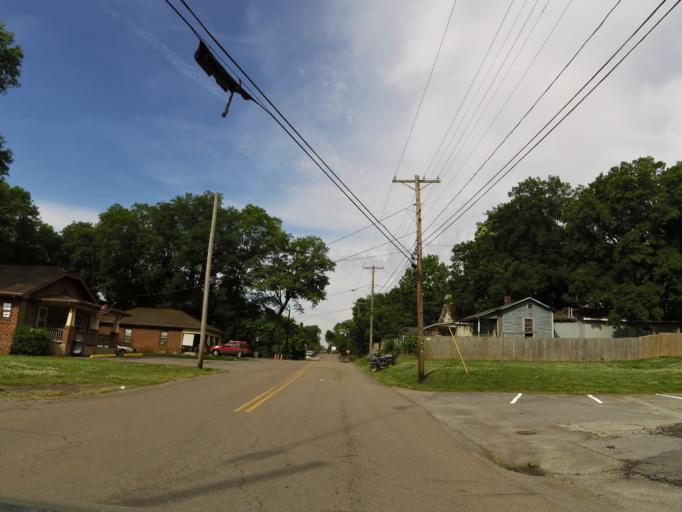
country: US
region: Tennessee
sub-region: Knox County
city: Knoxville
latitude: 35.9931
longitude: -83.9097
